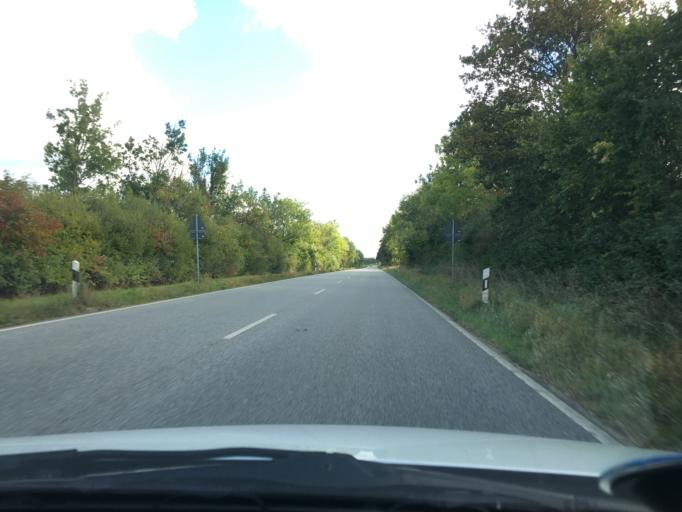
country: DE
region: Schleswig-Holstein
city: Krokau
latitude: 54.4018
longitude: 10.3734
